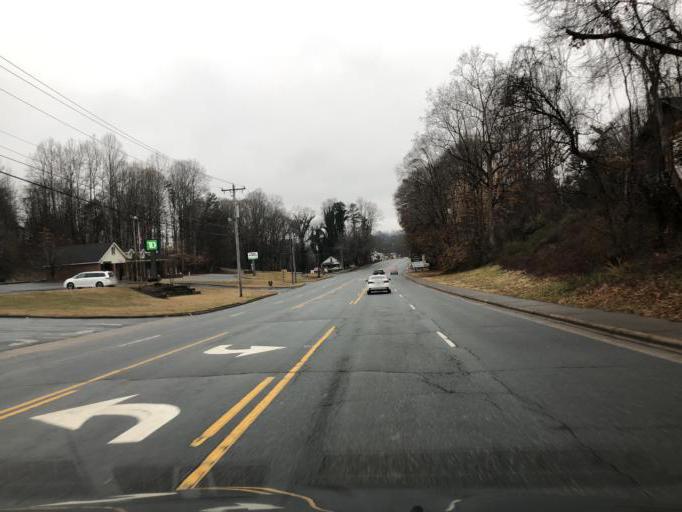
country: US
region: North Carolina
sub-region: Rutherford County
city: Rutherfordton
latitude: 35.3647
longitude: -81.9493
